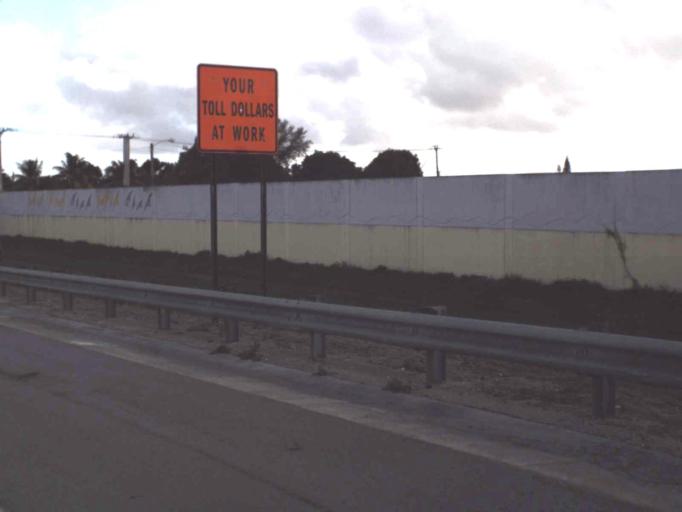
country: US
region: Florida
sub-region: Miami-Dade County
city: Scott Lake
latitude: 25.9397
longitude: -80.2208
